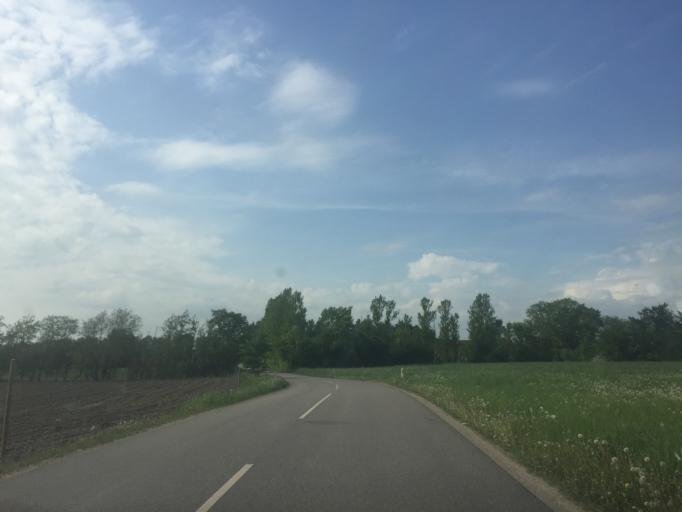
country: DK
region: Capital Region
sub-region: Egedal Kommune
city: Smorumnedre
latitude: 55.7153
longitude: 12.2783
